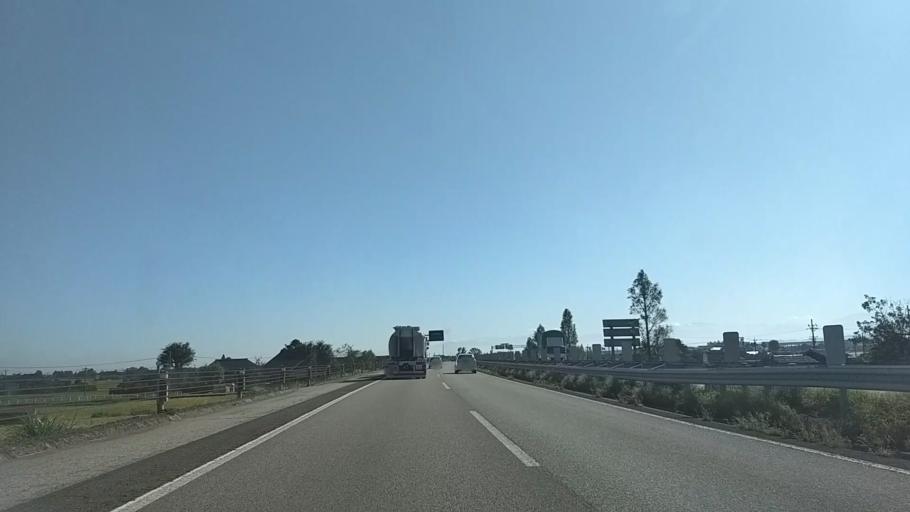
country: JP
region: Toyama
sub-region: Oyabe Shi
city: Oyabe
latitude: 36.6315
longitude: 136.8895
